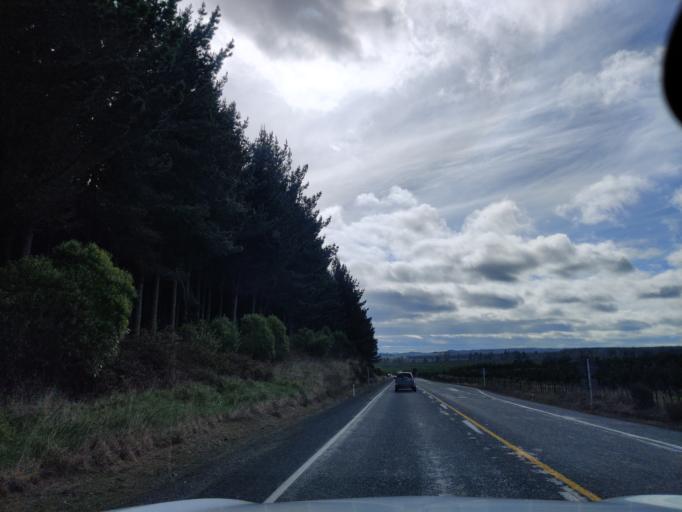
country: NZ
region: Waikato
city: Turangi
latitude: -39.0600
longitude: 175.8188
